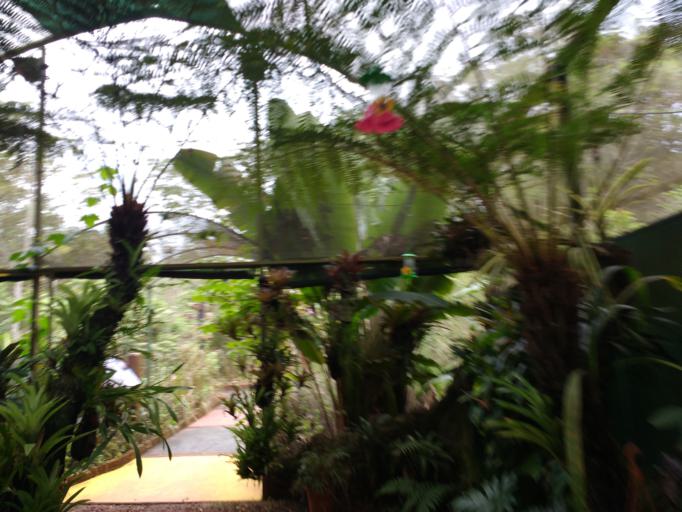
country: AR
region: Misiones
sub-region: Departamento de Iguazu
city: Puerto Iguazu
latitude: -25.6187
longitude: -54.5564
